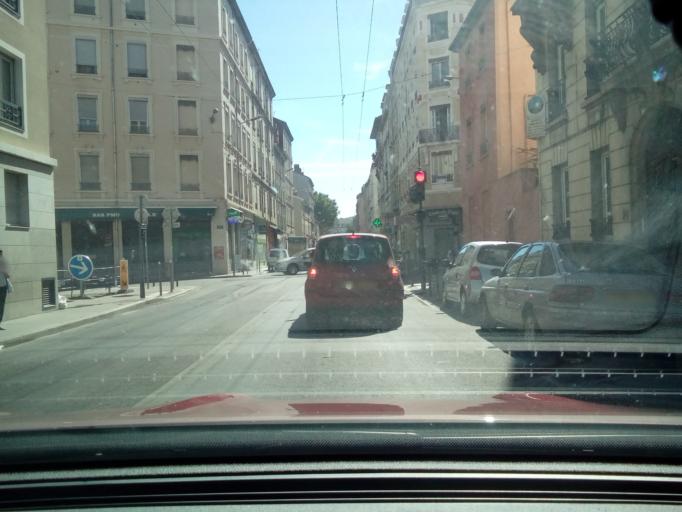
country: FR
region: Rhone-Alpes
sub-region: Departement du Rhone
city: Villeurbanne
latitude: 45.7610
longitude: 4.8843
